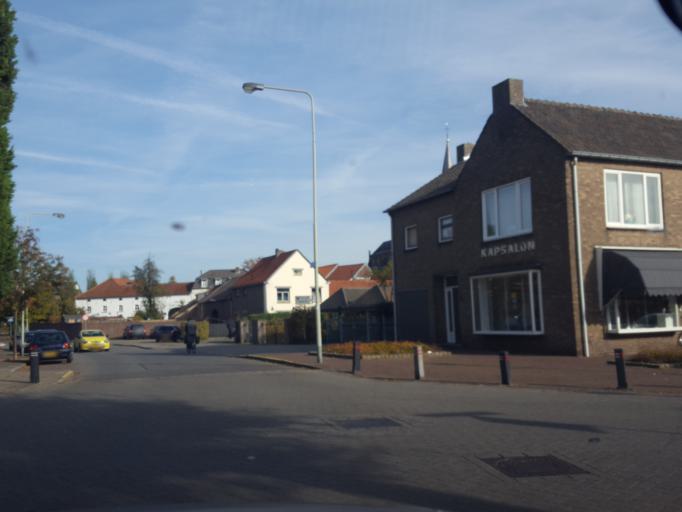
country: NL
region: Limburg
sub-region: Gemeente Schinnen
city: Puth
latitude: 50.9713
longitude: 5.8405
